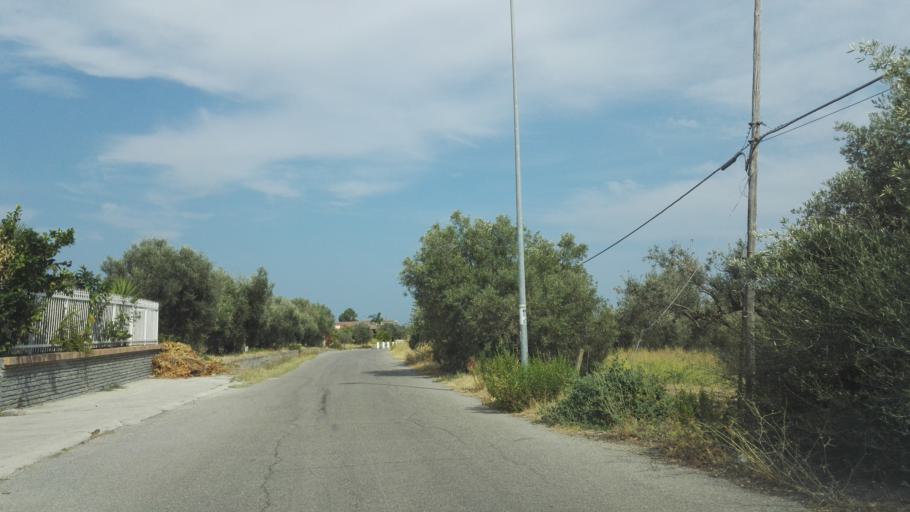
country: IT
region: Calabria
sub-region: Provincia di Reggio Calabria
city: Monasterace Marina
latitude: 38.4262
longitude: 16.5475
